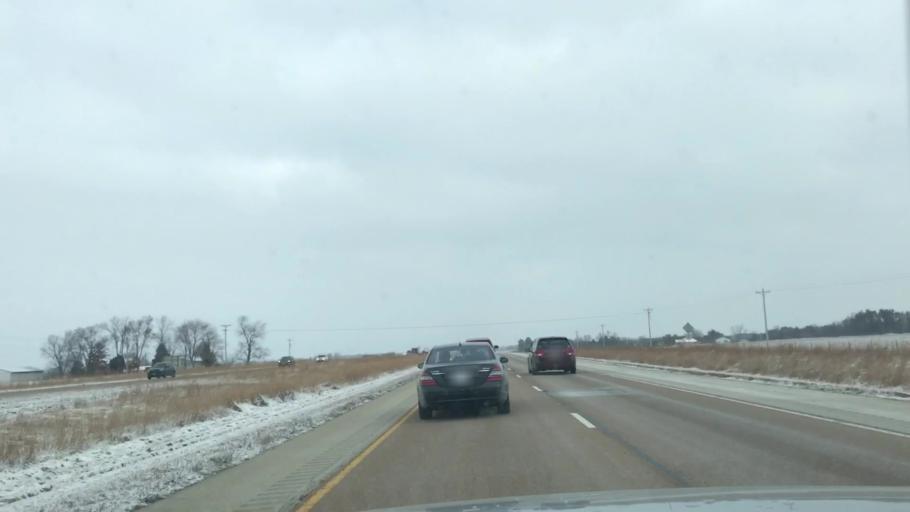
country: US
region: Illinois
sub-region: Montgomery County
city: Litchfield
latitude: 39.2391
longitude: -89.6411
